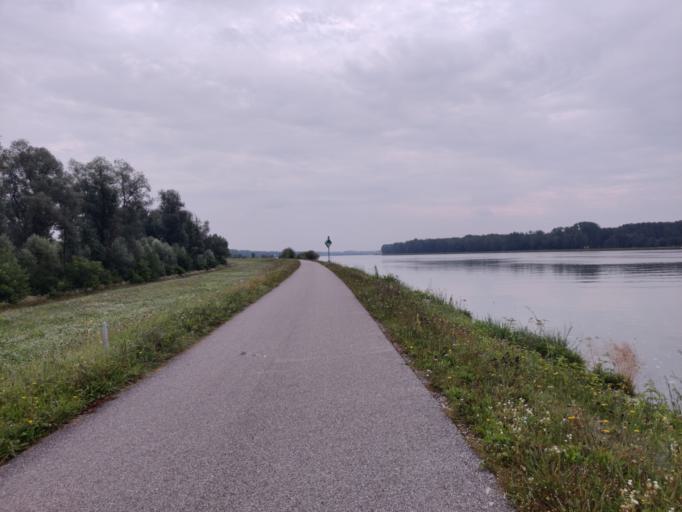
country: AT
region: Upper Austria
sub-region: Politischer Bezirk Urfahr-Umgebung
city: Steyregg
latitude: 48.2589
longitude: 14.4028
